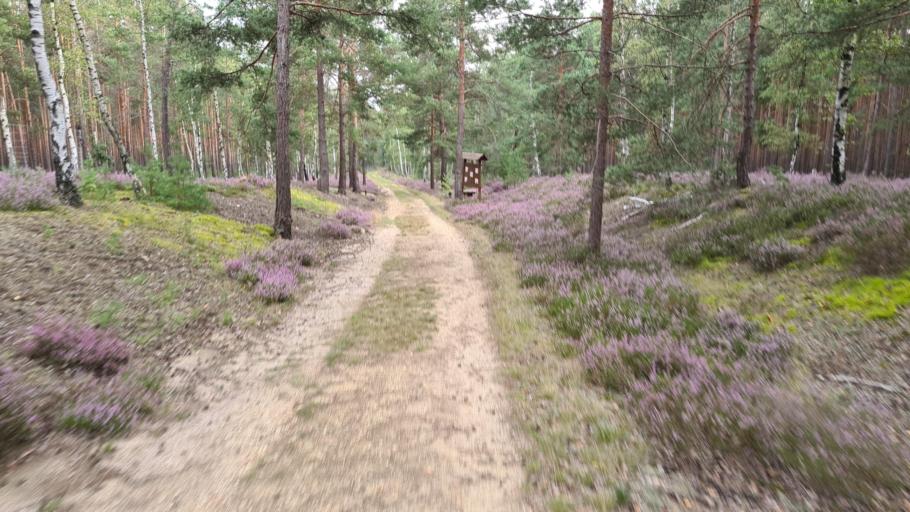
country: DE
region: Brandenburg
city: Schonborn
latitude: 51.6244
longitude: 13.4932
